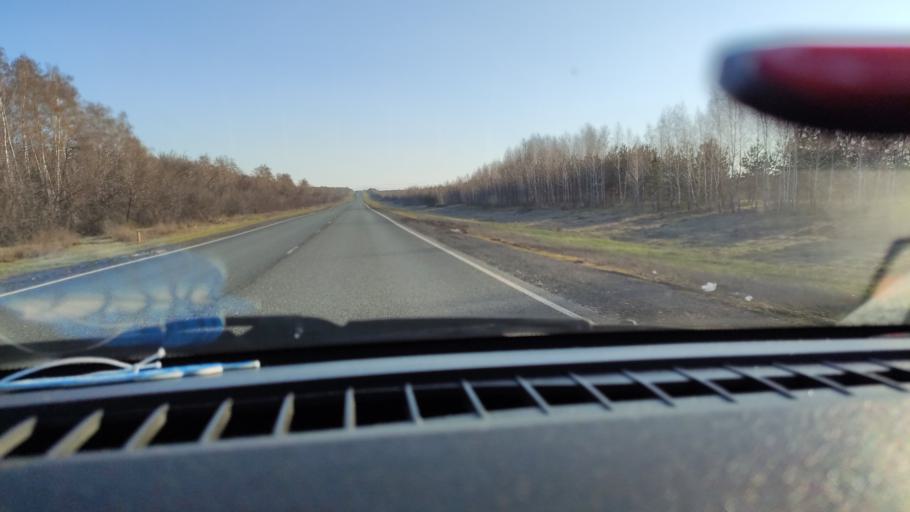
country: RU
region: Saratov
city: Balakovo
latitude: 52.1443
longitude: 47.8043
